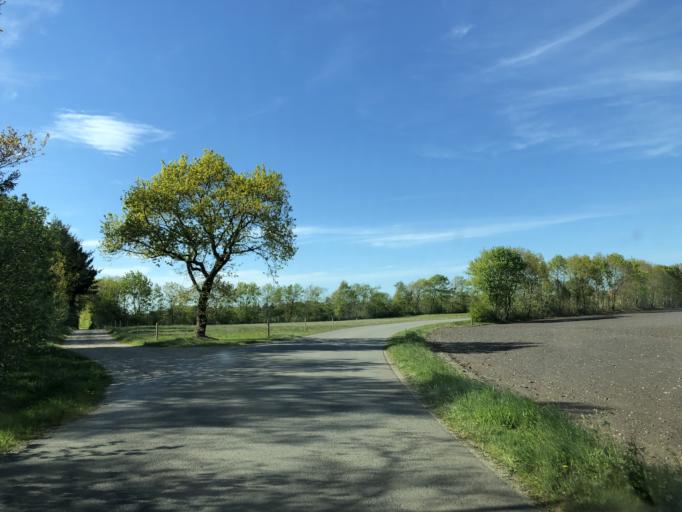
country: DK
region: Central Jutland
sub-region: Ringkobing-Skjern Kommune
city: Videbaek
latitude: 56.1885
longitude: 8.5157
